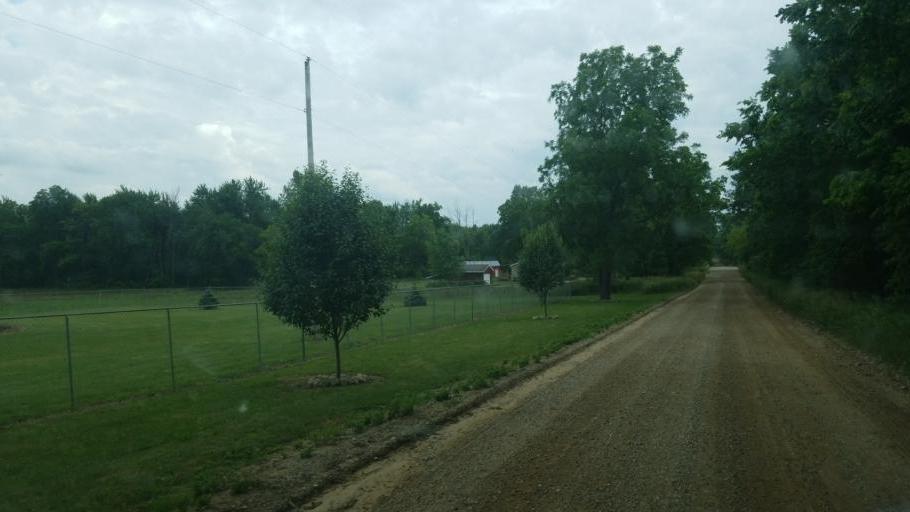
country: US
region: Michigan
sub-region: Barry County
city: Nashville
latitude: 42.6217
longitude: -84.9756
